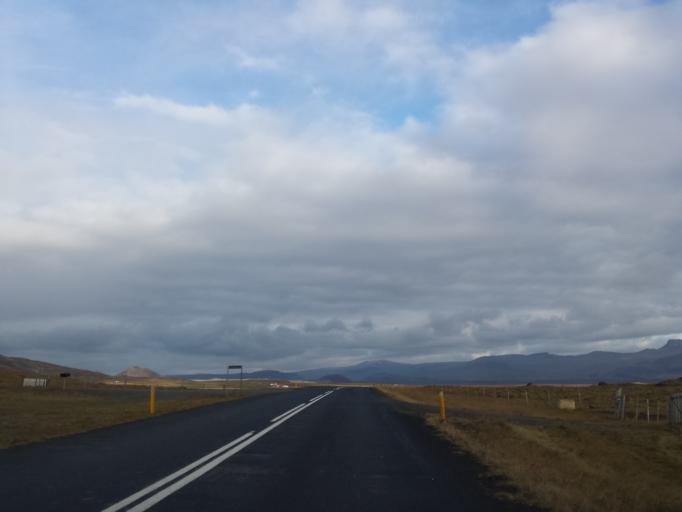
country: IS
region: West
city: Stykkisholmur
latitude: 64.8451
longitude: -22.4255
